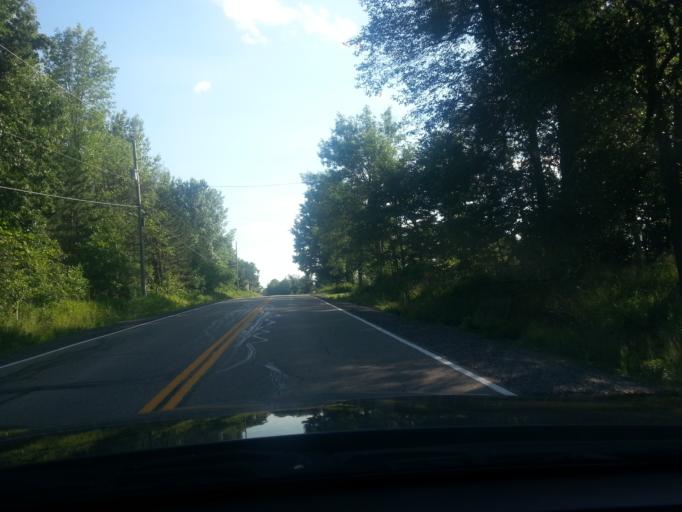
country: CA
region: Ontario
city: Carleton Place
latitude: 45.0643
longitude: -76.2832
